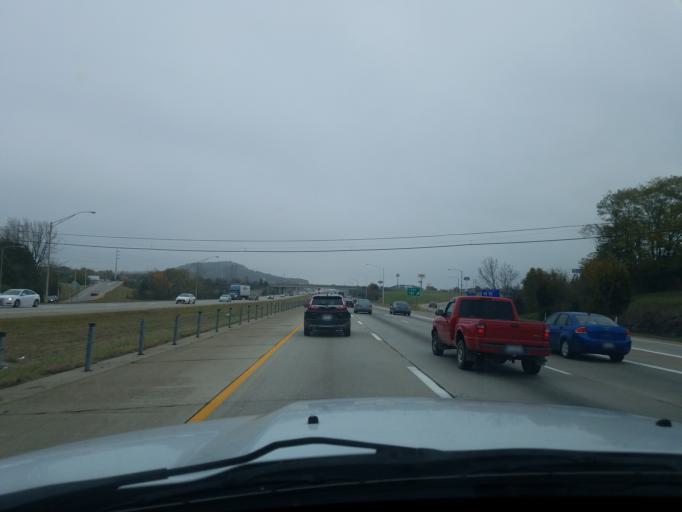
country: US
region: Kentucky
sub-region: Bullitt County
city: Brooks
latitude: 38.0593
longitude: -85.6989
